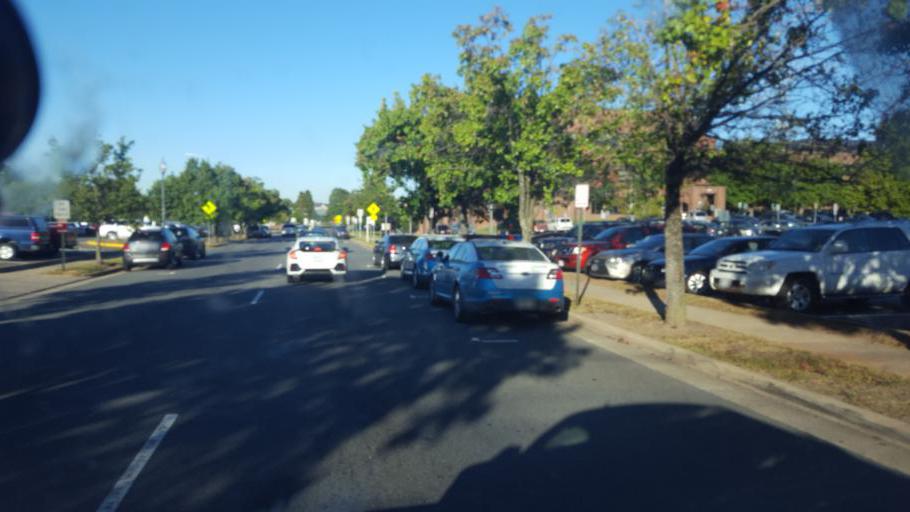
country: US
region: Virginia
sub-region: City of Manassas
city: Manassas
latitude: 38.7512
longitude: -77.4775
